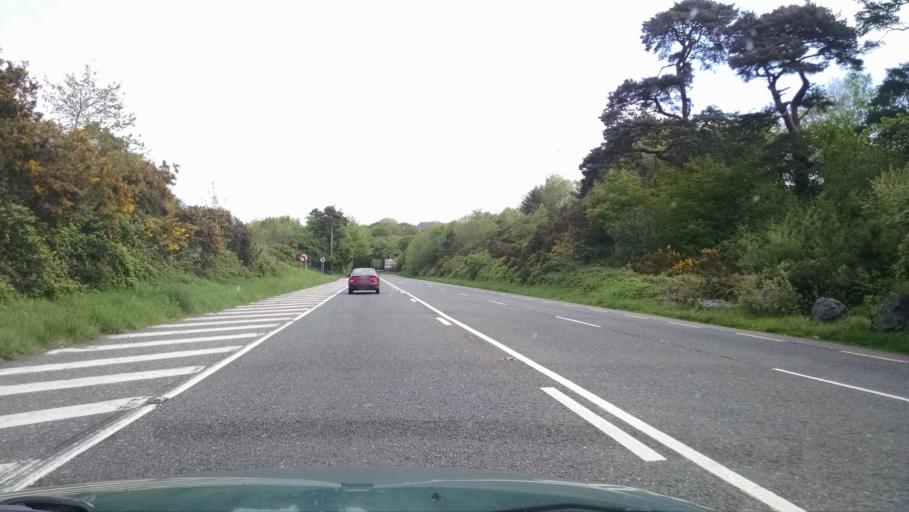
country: IE
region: Munster
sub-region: County Cork
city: Carrigaline
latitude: 51.8667
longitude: -8.4153
